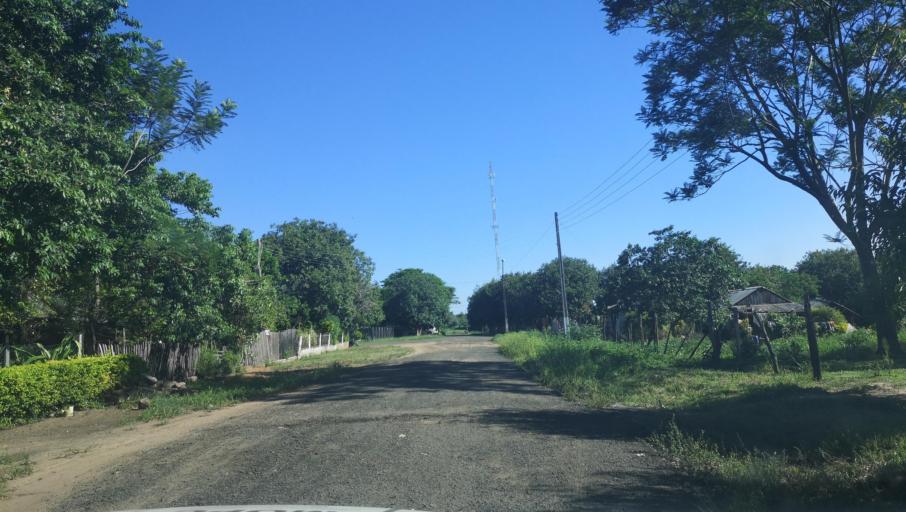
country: PY
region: Caaguazu
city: Carayao
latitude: -25.2042
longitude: -56.4005
